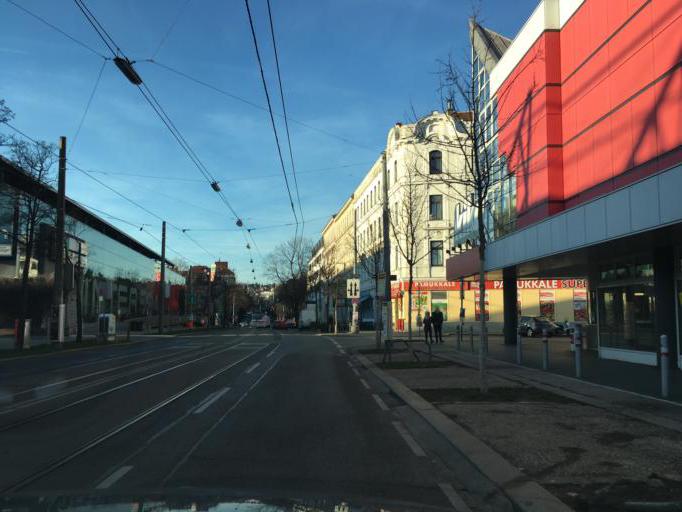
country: AT
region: Vienna
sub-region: Wien Stadt
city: Vienna
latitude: 48.2188
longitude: 16.3076
